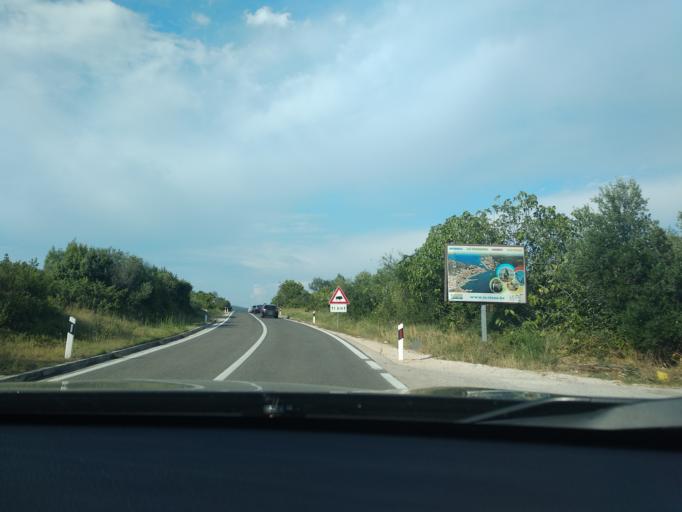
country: HR
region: Sibensko-Kniniska
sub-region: Grad Sibenik
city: Pirovac
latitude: 43.8028
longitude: 15.6634
